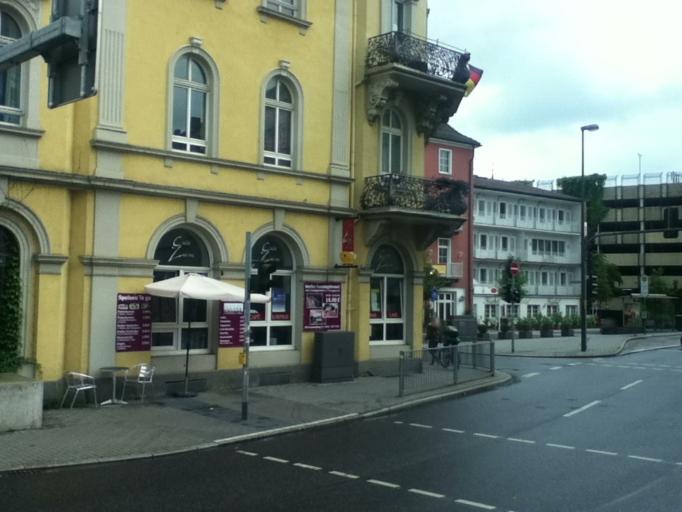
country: DE
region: Hesse
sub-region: Regierungsbezirk Giessen
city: Giessen
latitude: 50.5840
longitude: 8.6686
